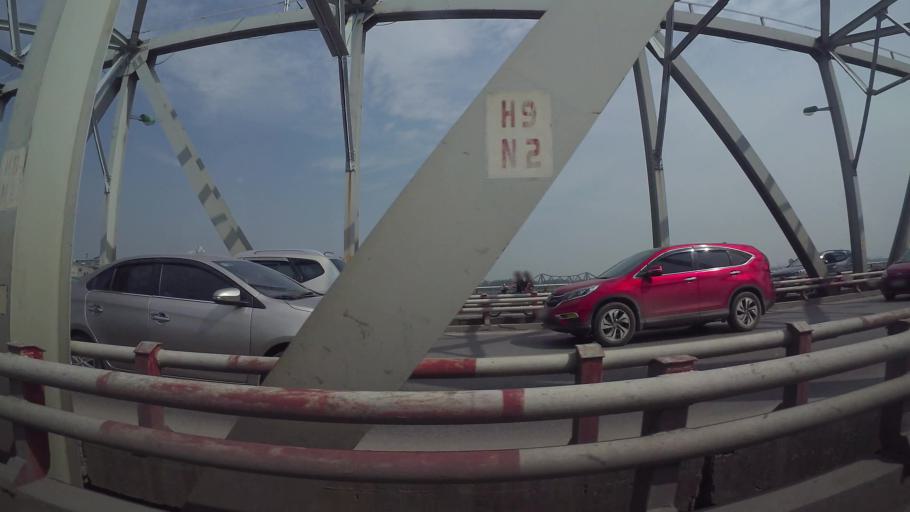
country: VN
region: Ha Noi
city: Hoan Kiem
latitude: 21.0363
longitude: 105.8583
